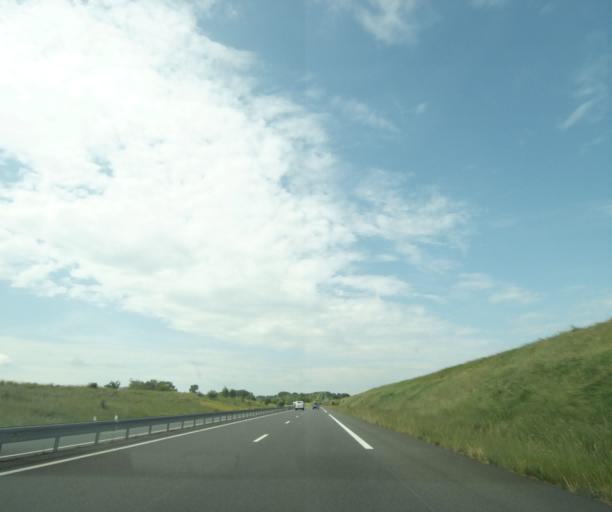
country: FR
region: Pays de la Loire
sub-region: Departement de Maine-et-Loire
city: Saint-Philbert-du-Peuple
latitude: 47.3731
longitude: -0.0844
